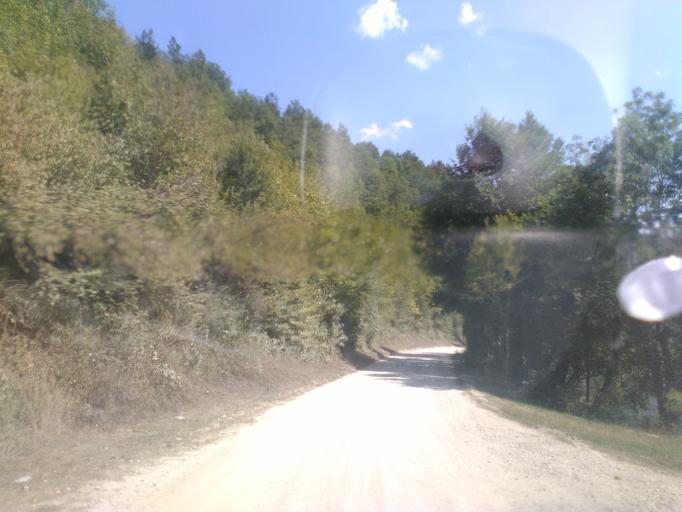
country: BA
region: Federation of Bosnia and Herzegovina
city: Orasac
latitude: 44.6262
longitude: 16.0544
